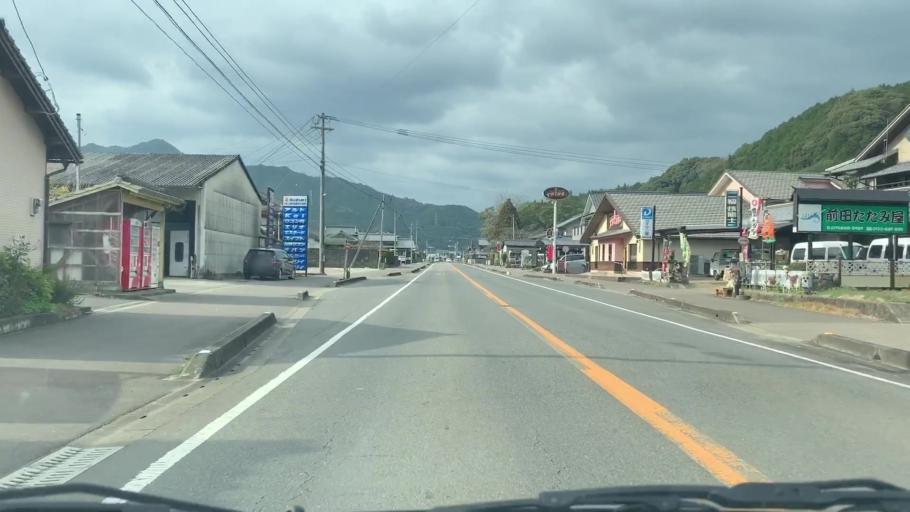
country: JP
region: Saga Prefecture
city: Ureshinomachi-shimojuku
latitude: 33.1264
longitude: 130.0439
